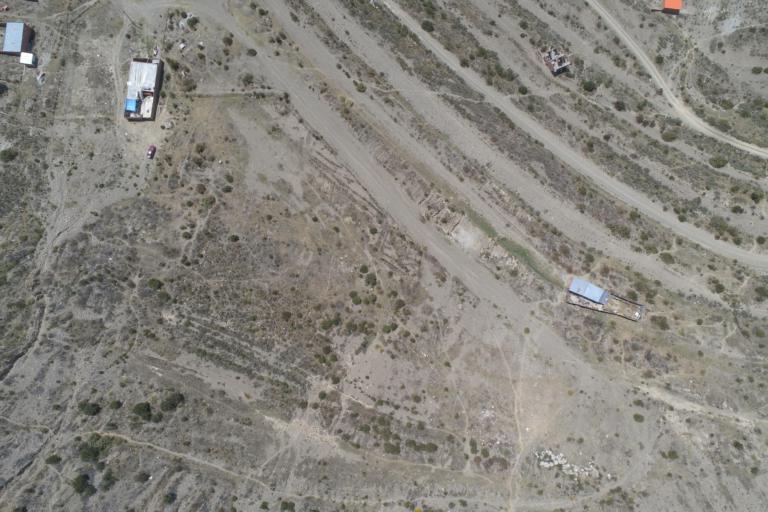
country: BO
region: La Paz
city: La Paz
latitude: -16.5027
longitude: -68.0995
